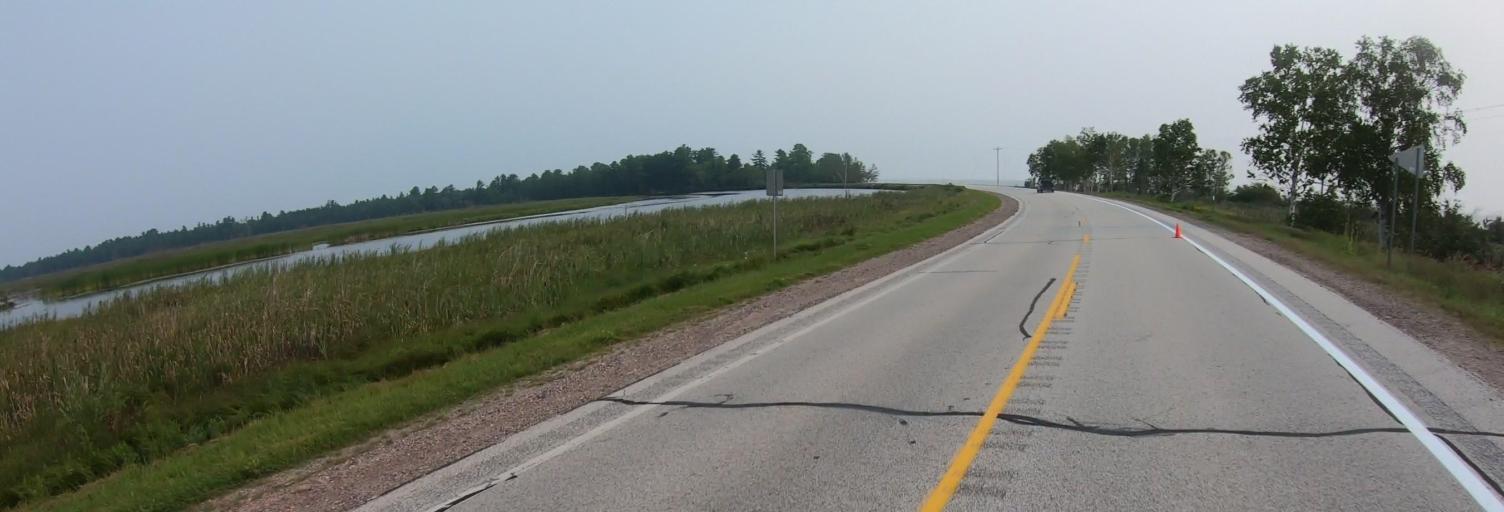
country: US
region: Michigan
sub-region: Luce County
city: Newberry
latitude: 46.5584
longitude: -85.0296
